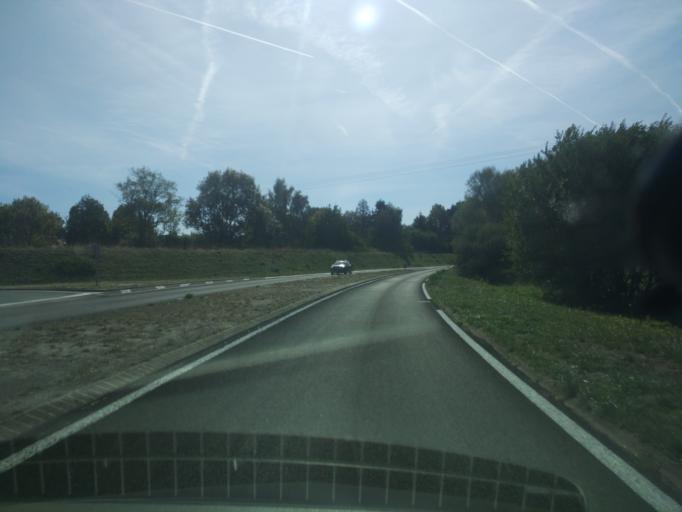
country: FR
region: Ile-de-France
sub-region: Departement de l'Essonne
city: Briis-sous-Forges
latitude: 48.6283
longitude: 2.1176
